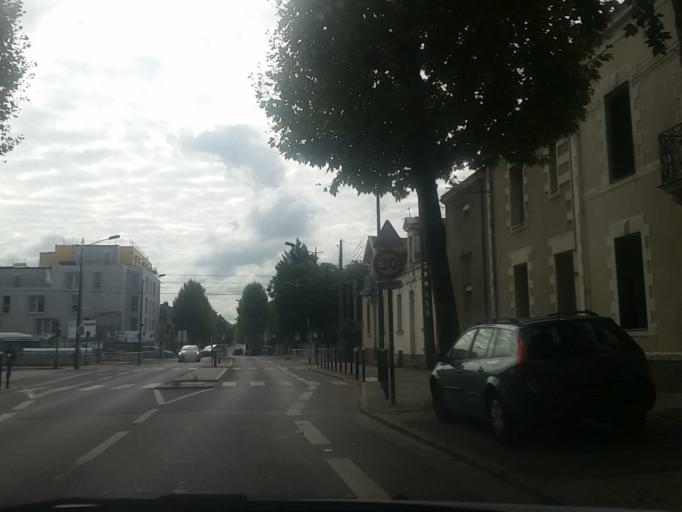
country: FR
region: Pays de la Loire
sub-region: Departement de la Loire-Atlantique
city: Saint-Sebastien-sur-Loire
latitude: 47.2245
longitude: -1.5209
